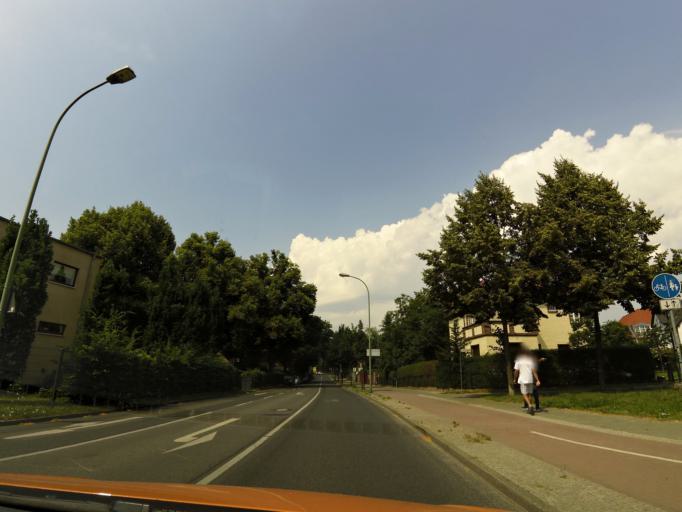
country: DE
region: Brandenburg
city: Potsdam
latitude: 52.4137
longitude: 13.0317
